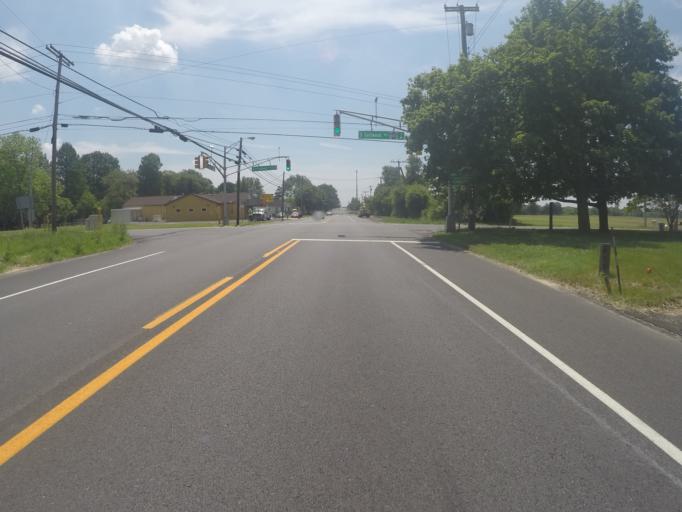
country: US
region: New Jersey
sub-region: Salem County
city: Carneys Point
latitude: 39.7127
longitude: -75.4505
